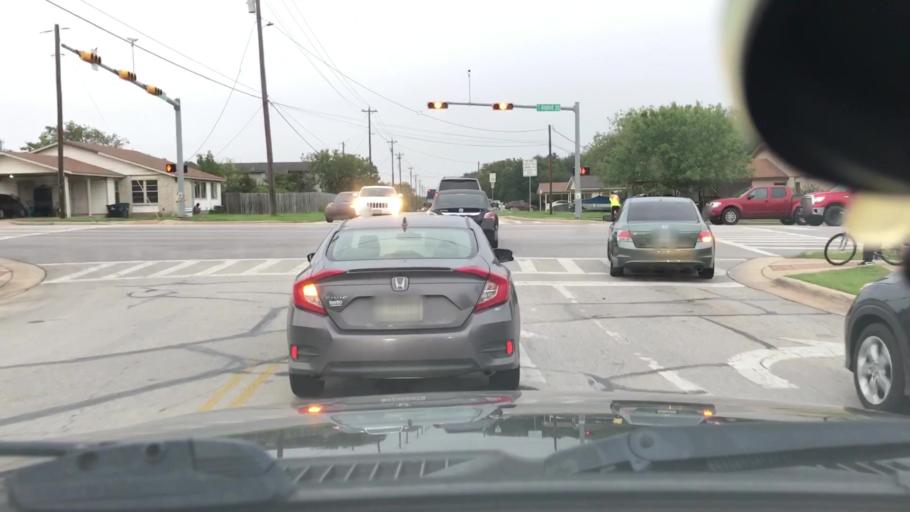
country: US
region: Texas
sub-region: Williamson County
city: Leander
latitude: 30.5415
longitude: -97.8502
